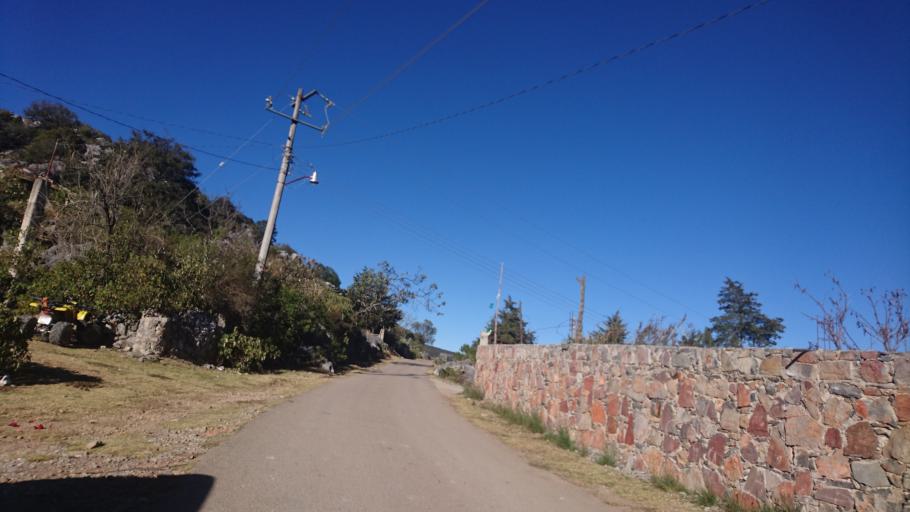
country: MX
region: San Luis Potosi
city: Zaragoza
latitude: 22.0212
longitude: -100.6022
